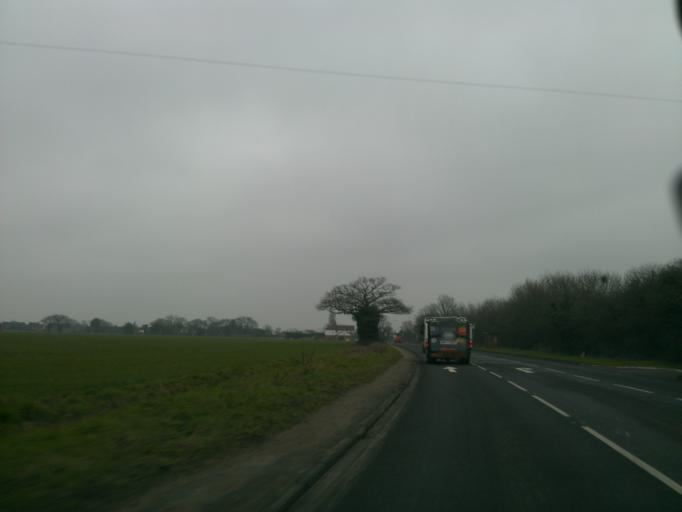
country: GB
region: England
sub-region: Essex
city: Alresford
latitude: 51.8681
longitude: 1.0259
